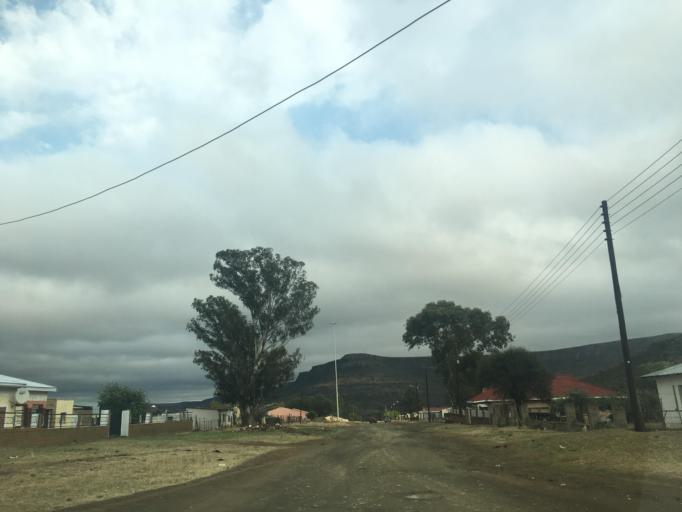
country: ZA
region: Eastern Cape
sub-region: Chris Hani District Municipality
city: Cala
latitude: -31.5197
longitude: 27.6958
